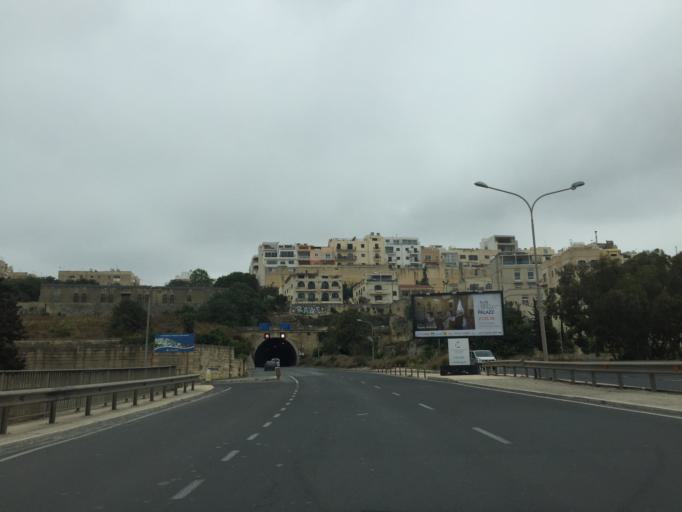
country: MT
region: Saint Julian
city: San Giljan
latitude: 35.9161
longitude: 14.4862
